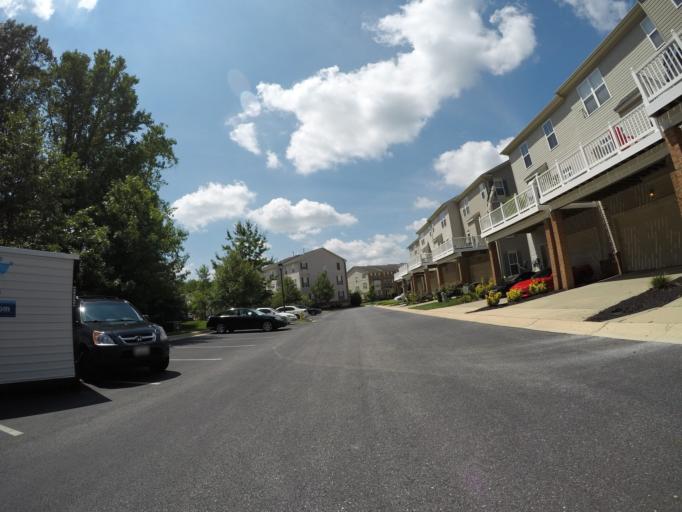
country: US
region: Maryland
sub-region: Anne Arundel County
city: Odenton
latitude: 39.0500
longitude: -76.7057
